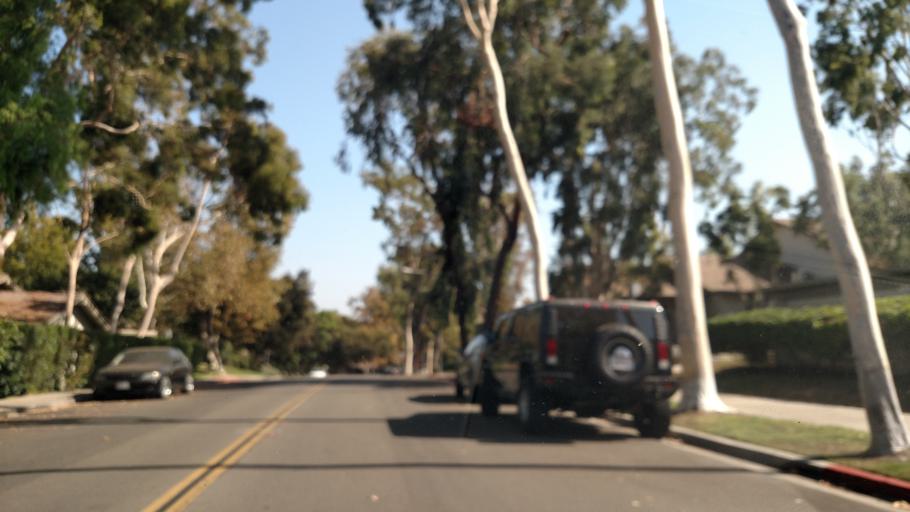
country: US
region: California
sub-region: Orange County
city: Irvine
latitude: 33.6589
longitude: -117.8329
